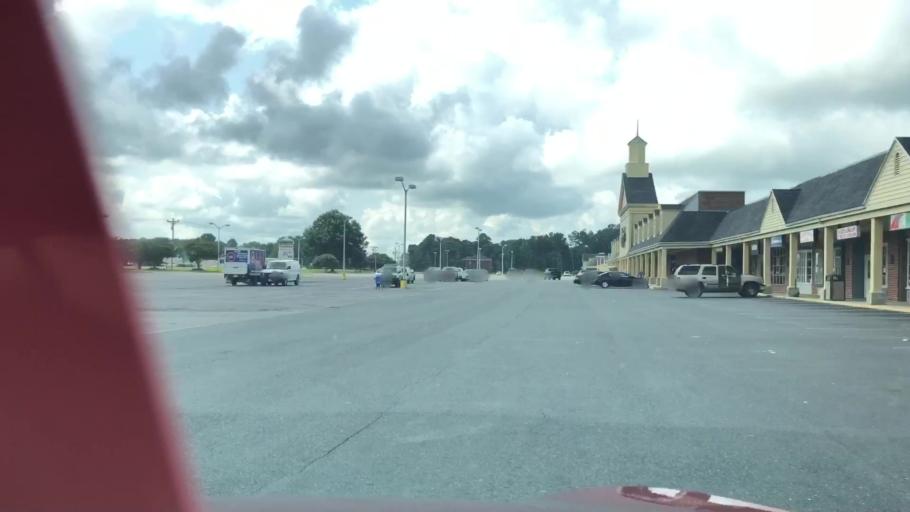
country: US
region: Virginia
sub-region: Accomack County
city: Onancock
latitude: 37.6980
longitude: -75.7189
